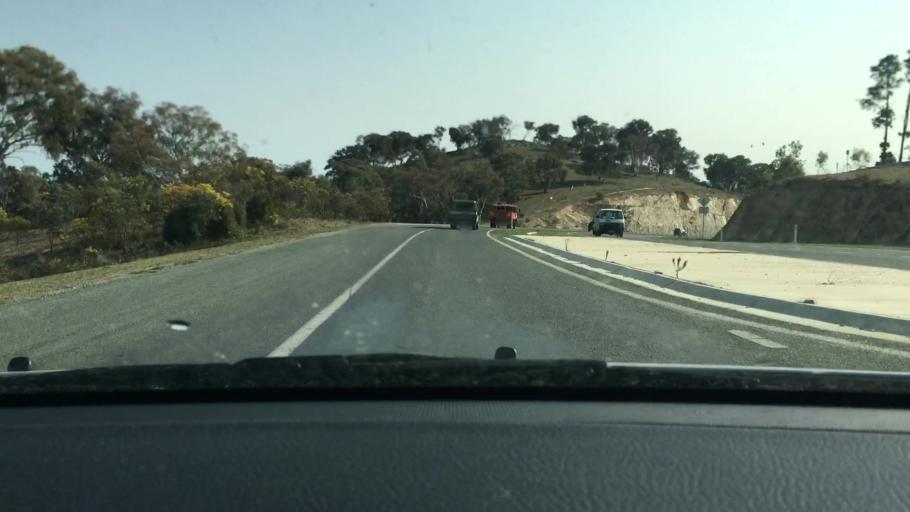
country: AU
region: New South Wales
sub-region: Queanbeyan
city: Queanbeyan
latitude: -35.4016
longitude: 149.2304
